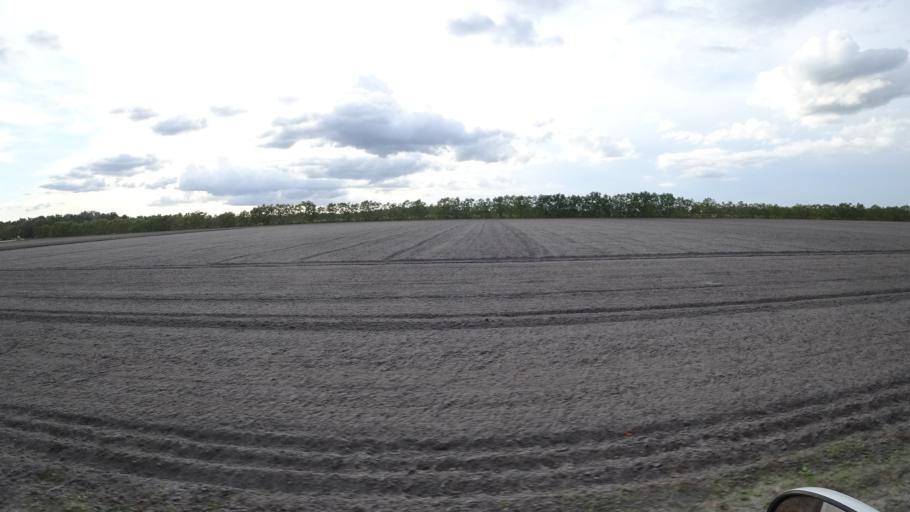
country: US
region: Florida
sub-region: Hillsborough County
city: Wimauma
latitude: 27.5685
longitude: -82.0821
